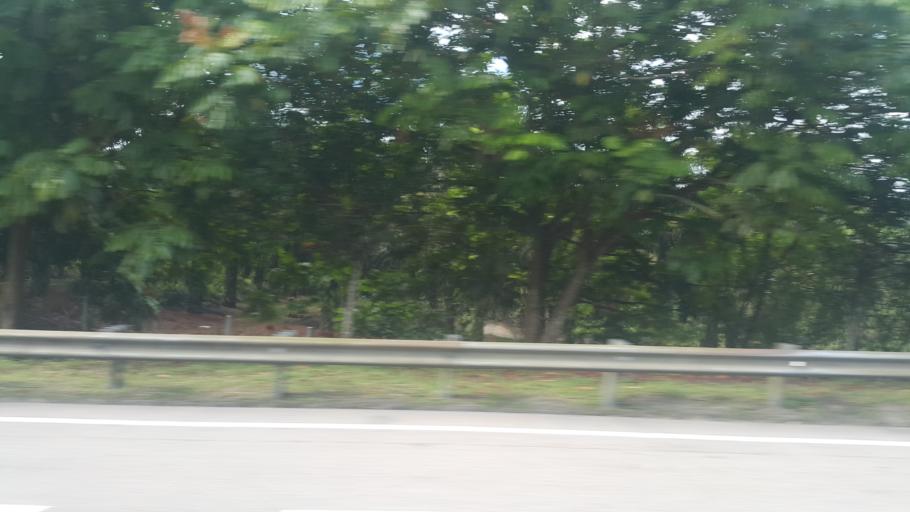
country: MY
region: Johor
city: Taman Senai
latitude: 1.6076
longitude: 103.6132
